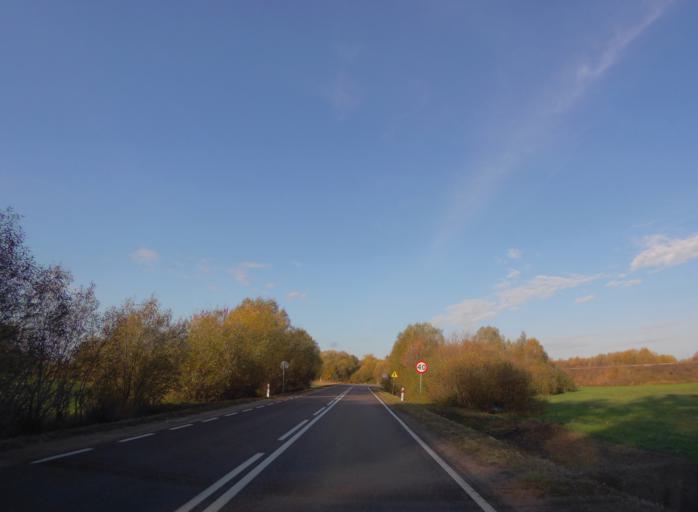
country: PL
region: Masovian Voivodeship
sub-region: Powiat siedlecki
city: Mordy
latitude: 52.2168
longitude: 22.5689
